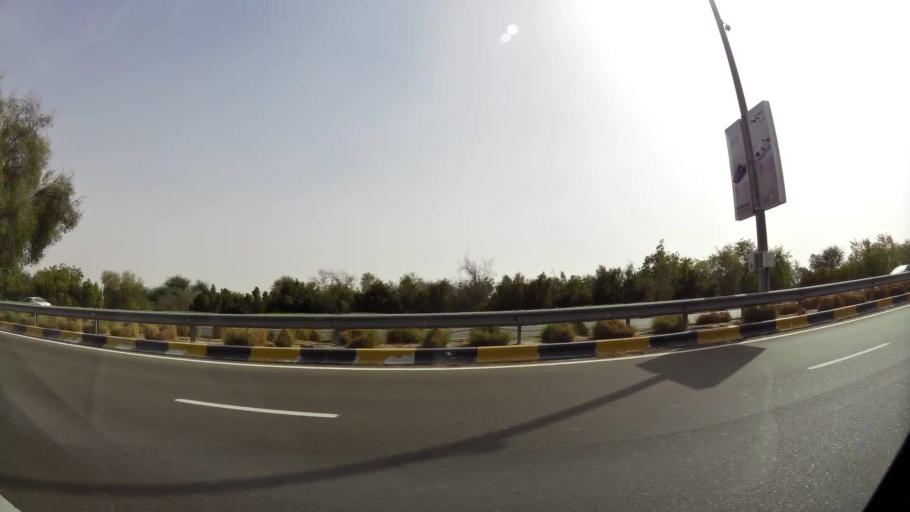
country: AE
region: Abu Dhabi
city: Al Ain
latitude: 24.1791
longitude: 55.6010
